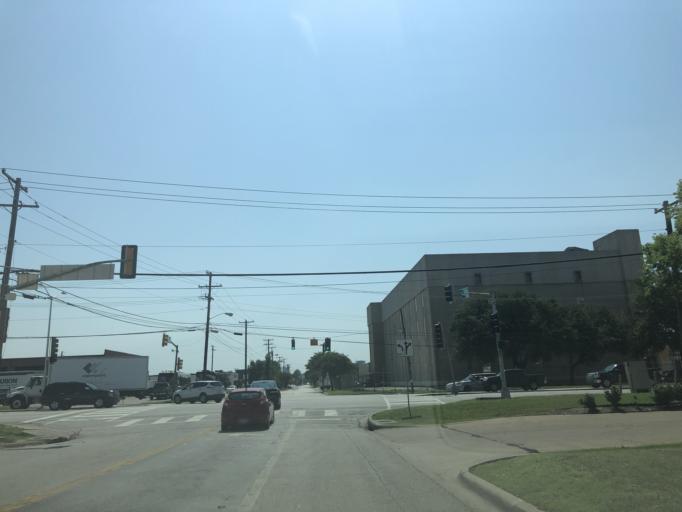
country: US
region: Texas
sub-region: Dallas County
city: Dallas
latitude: 32.8120
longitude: -96.8741
